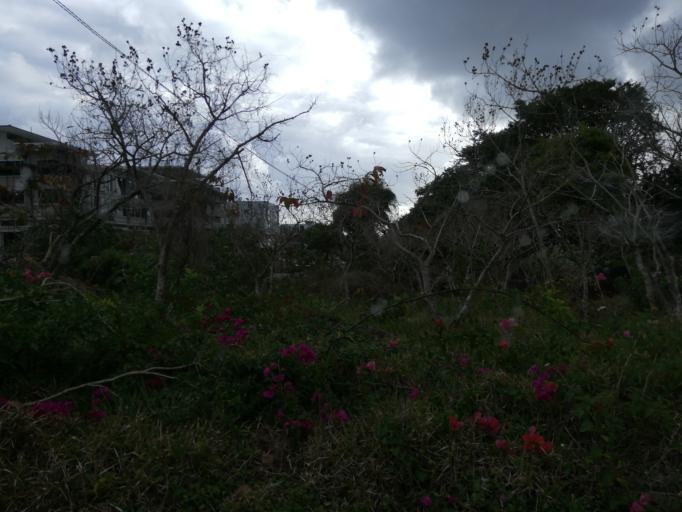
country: MU
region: Plaines Wilhems
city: Ebene
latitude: -20.2420
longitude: 57.4845
